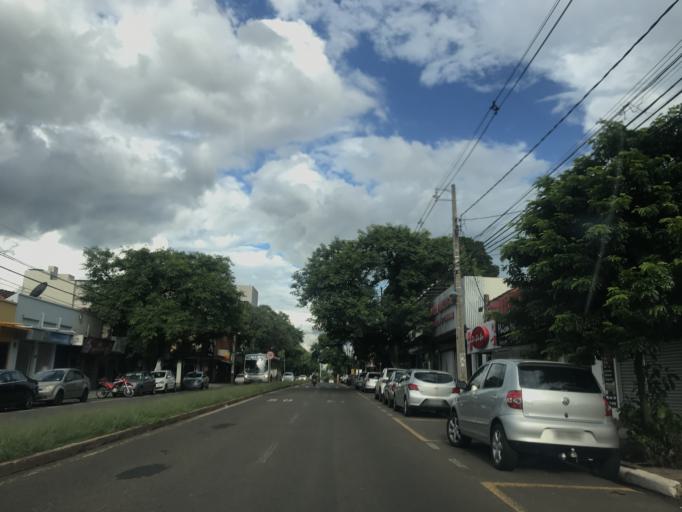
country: BR
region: Parana
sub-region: Maringa
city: Maringa
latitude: -23.4236
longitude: -51.9568
